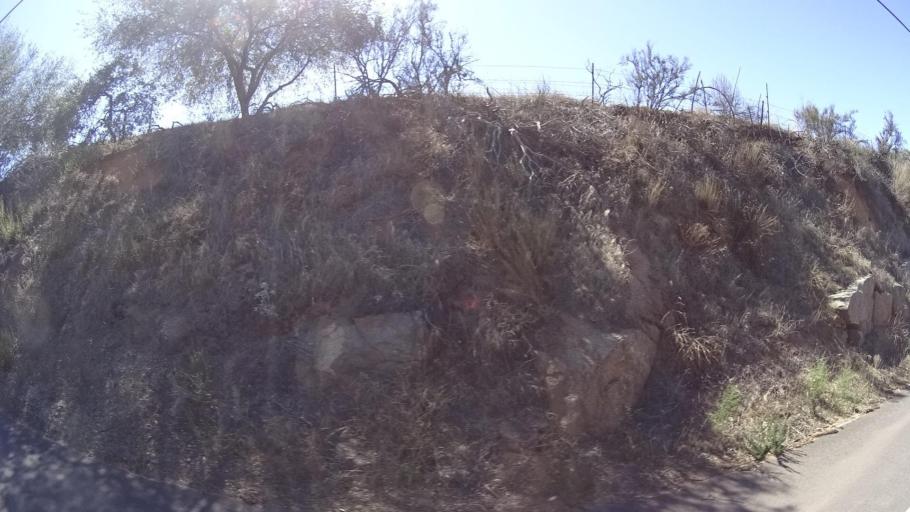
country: US
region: California
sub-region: San Diego County
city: Alpine
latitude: 32.7650
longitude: -116.6896
